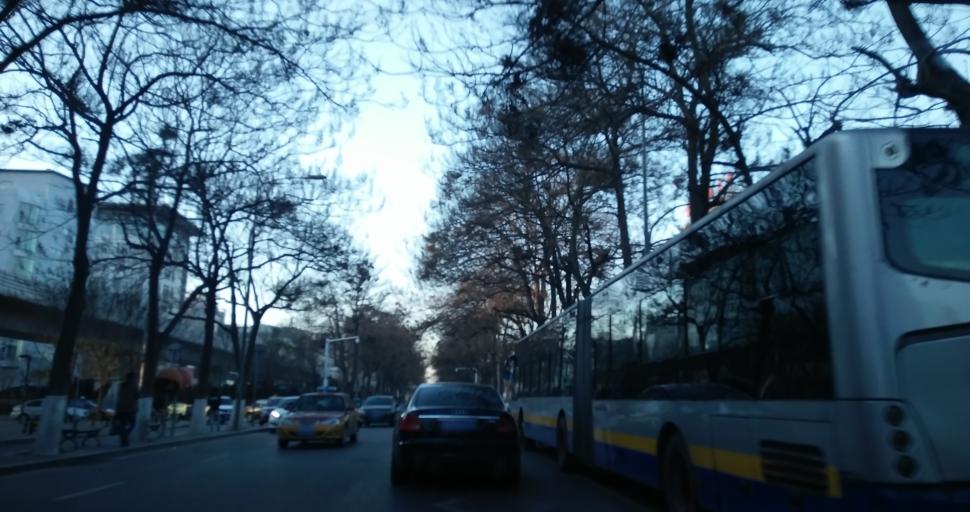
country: CN
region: Beijing
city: Jiugong
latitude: 39.7821
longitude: 116.5159
